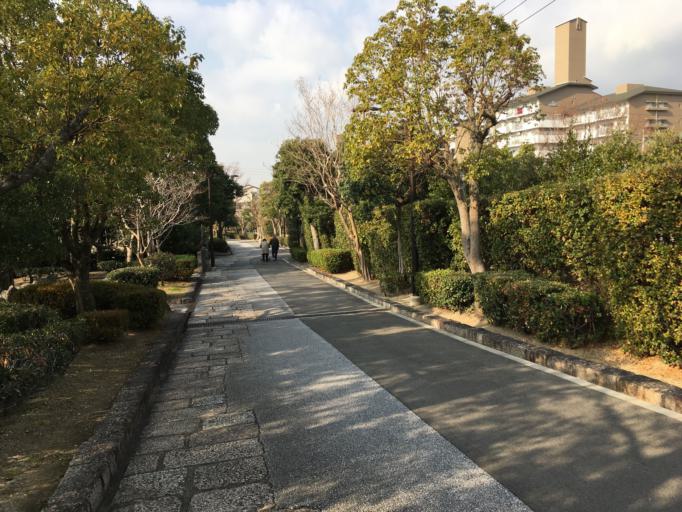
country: JP
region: Hyogo
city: Ashiya
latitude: 34.7195
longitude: 135.3128
